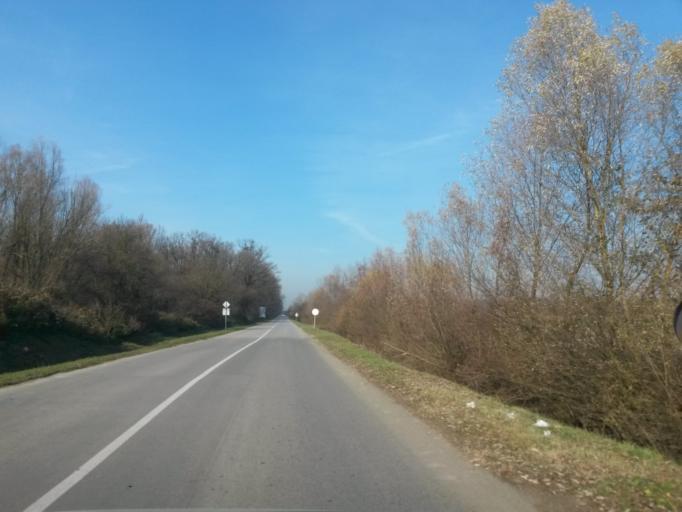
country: HR
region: Vukovarsko-Srijemska
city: Privlaka
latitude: 45.2140
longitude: 18.8584
